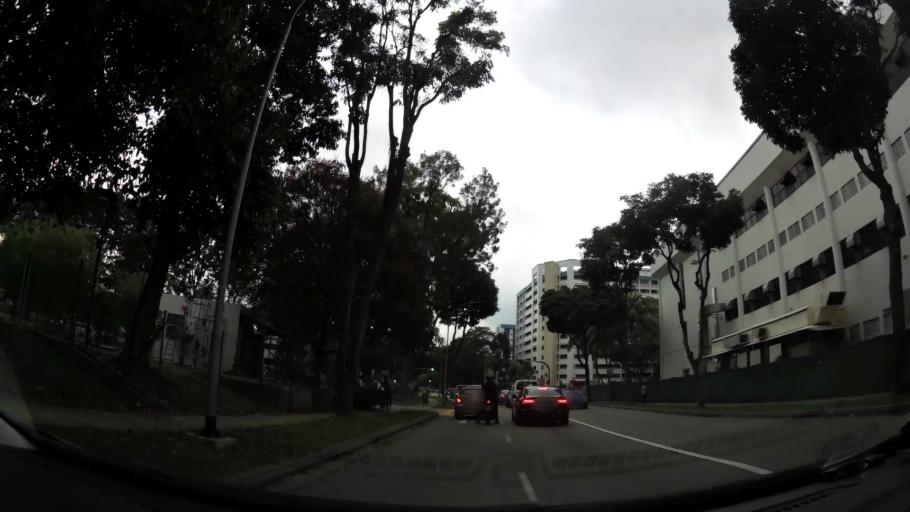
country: MY
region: Johor
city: Kampung Pasir Gudang Baru
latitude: 1.4417
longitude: 103.8391
